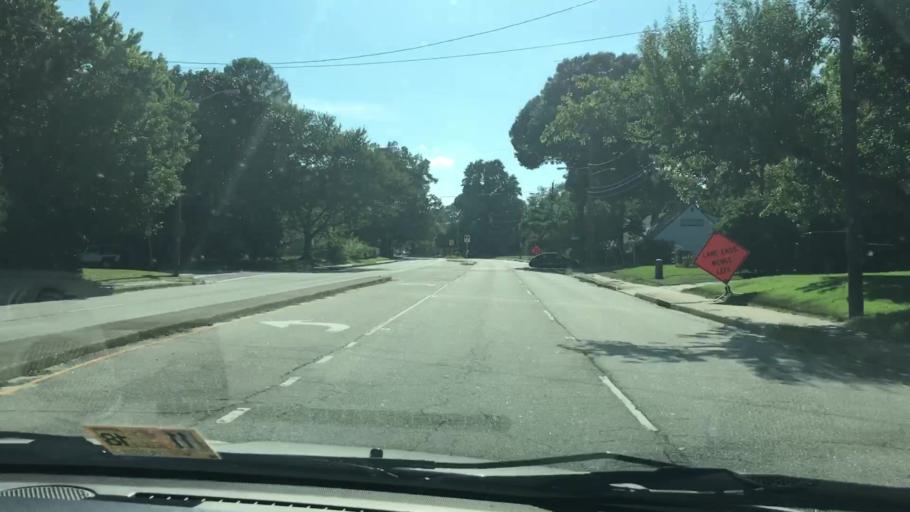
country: US
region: Virginia
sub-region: City of Norfolk
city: Norfolk
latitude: 36.8969
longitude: -76.2185
